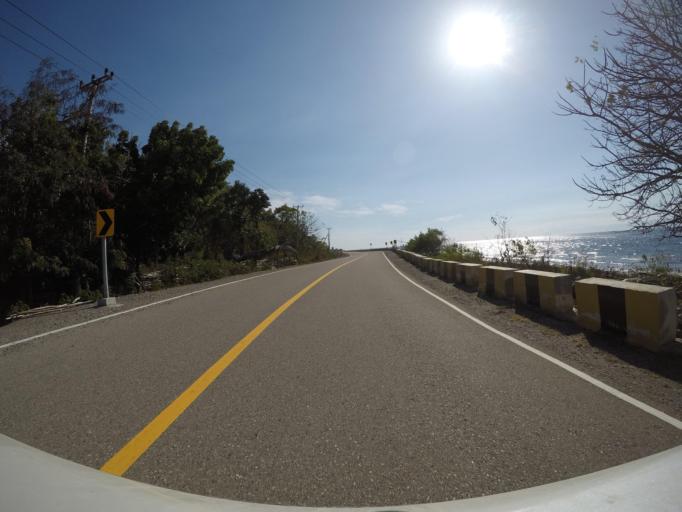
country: TL
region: Liquica
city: Maubara
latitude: -8.6133
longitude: 125.1916
